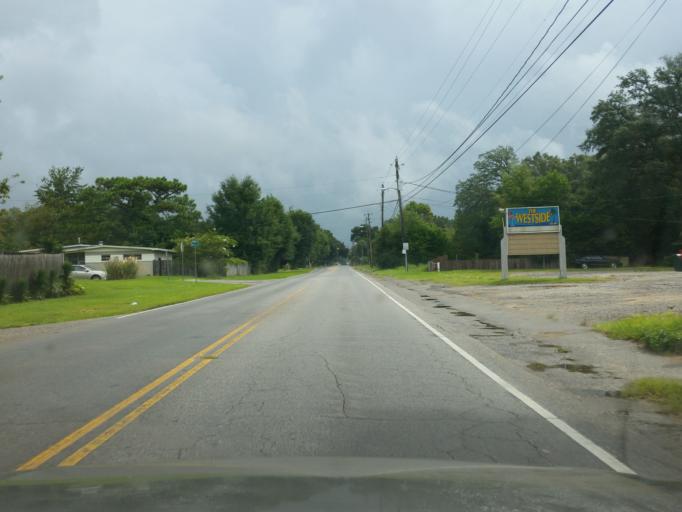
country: US
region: Florida
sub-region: Escambia County
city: West Pensacola
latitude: 30.4515
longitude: -87.2650
